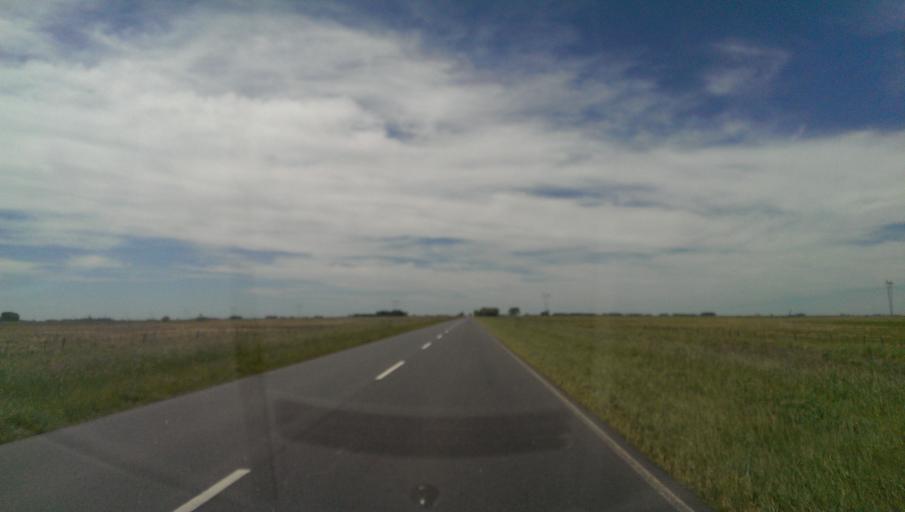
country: AR
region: Buenos Aires
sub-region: Partido de Laprida
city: Laprida
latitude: -37.2367
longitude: -60.7337
